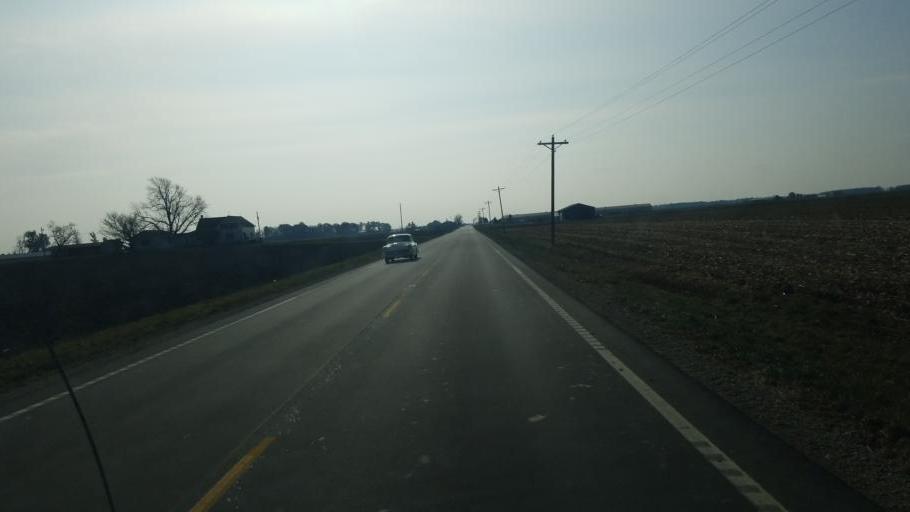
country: US
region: Ohio
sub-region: Mercer County
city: Fort Recovery
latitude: 40.4915
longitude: -84.7844
